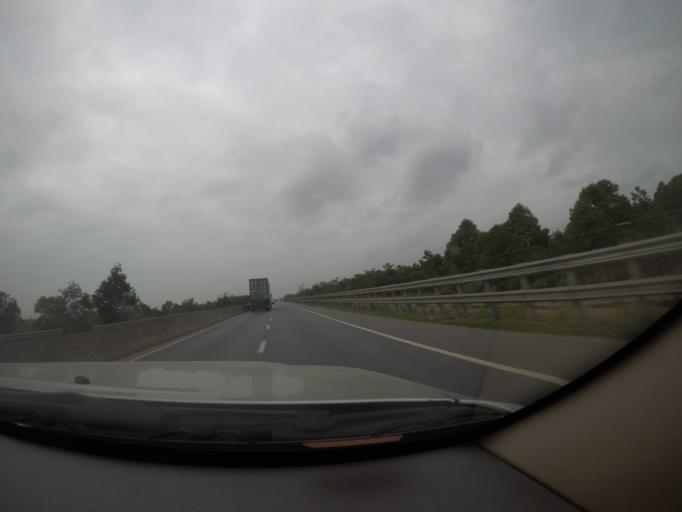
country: VN
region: Quang Tri
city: Hai Lang
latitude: 16.6494
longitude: 107.2868
